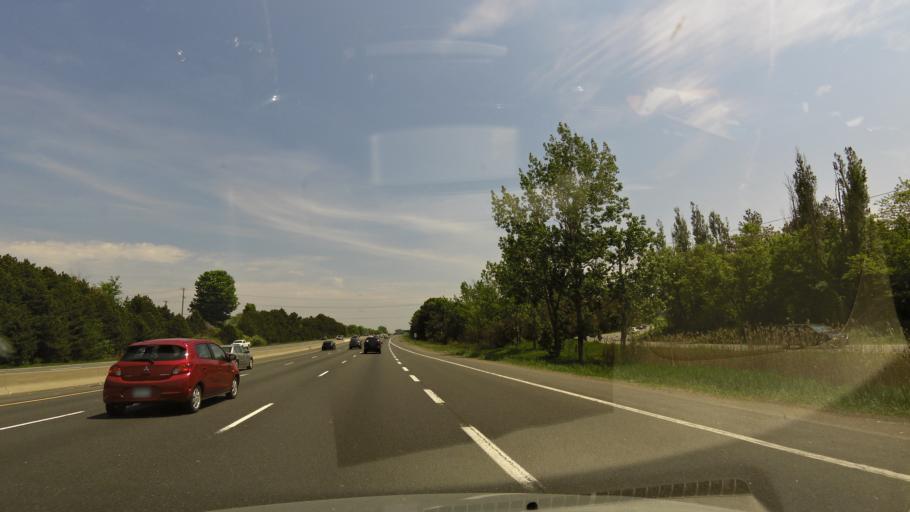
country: CA
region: Ontario
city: Oshawa
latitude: 43.8992
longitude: -78.6718
